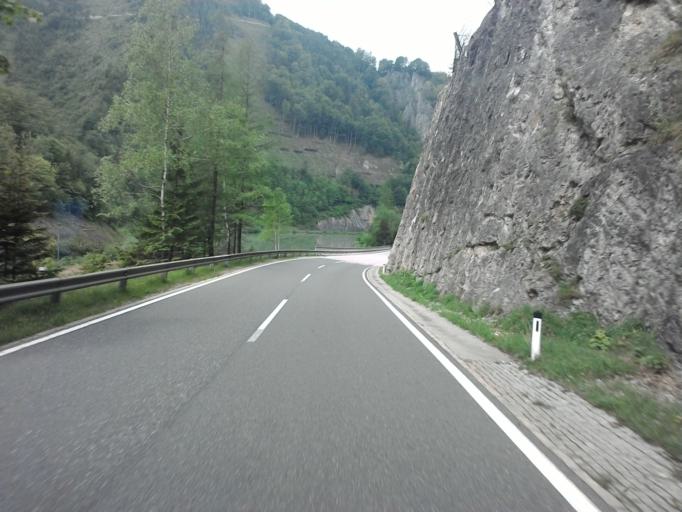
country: AT
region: Styria
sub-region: Politischer Bezirk Liezen
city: Altenmarkt bei Sankt Gallen
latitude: 47.7717
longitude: 14.6534
